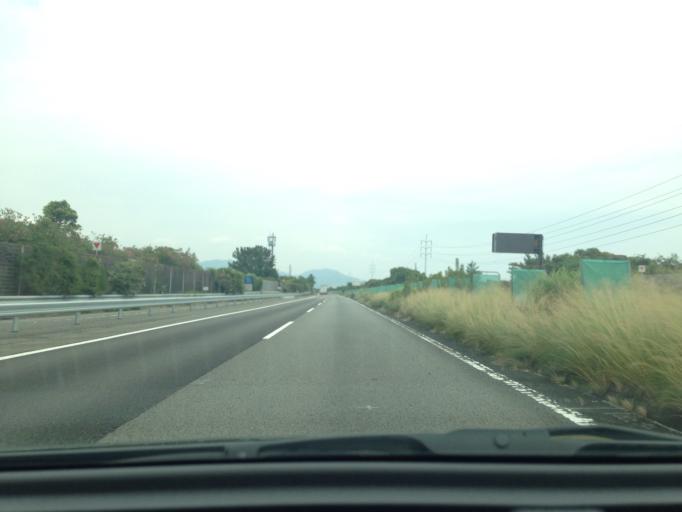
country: JP
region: Shizuoka
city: Fujieda
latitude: 34.8218
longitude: 138.2693
